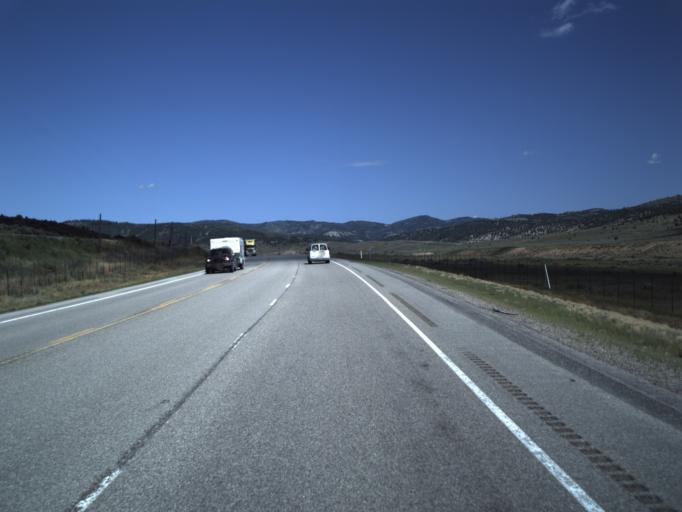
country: US
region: Utah
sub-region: Carbon County
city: Helper
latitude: 39.8916
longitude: -111.0516
